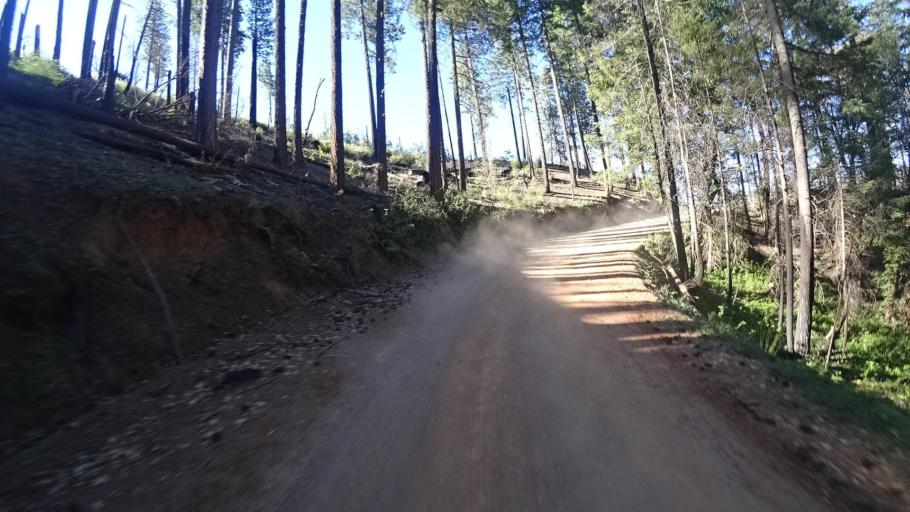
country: US
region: California
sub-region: Lake County
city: Upper Lake
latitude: 39.3755
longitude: -122.9907
